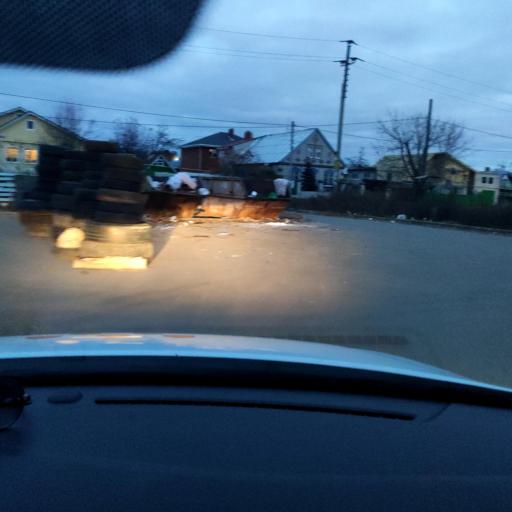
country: RU
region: Tatarstan
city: Staroye Arakchino
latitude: 55.8701
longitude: 49.0268
